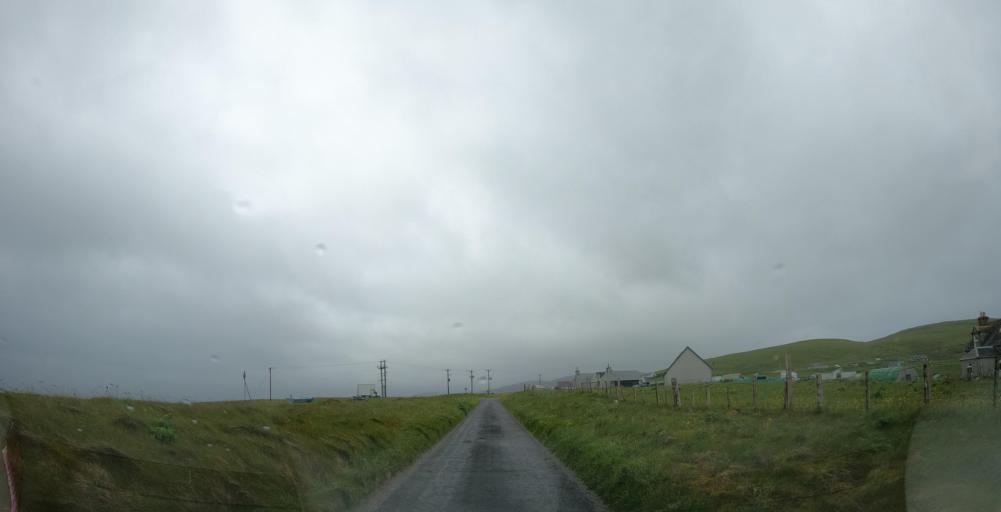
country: GB
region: Scotland
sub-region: Eilean Siar
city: Barra
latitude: 57.0407
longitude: -7.4241
